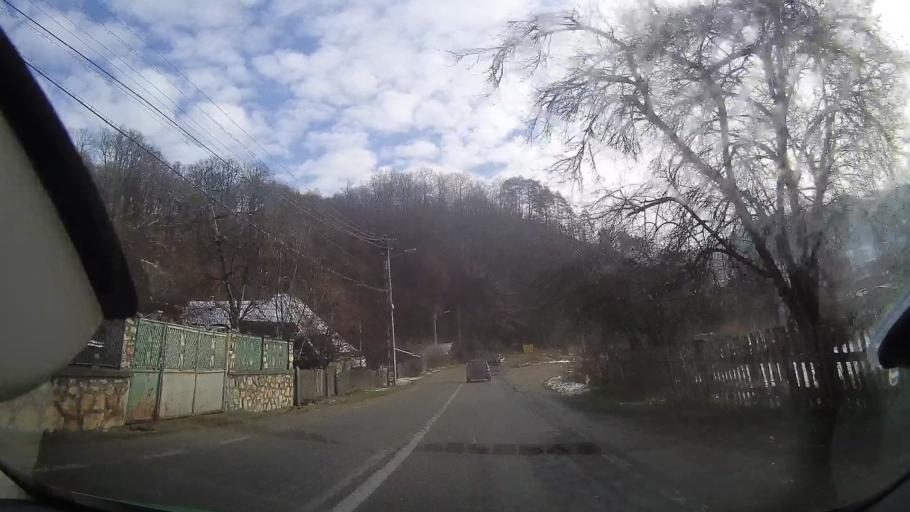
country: RO
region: Alba
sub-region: Oras Baia de Aries
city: Baia de Aries
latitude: 46.3827
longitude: 23.2775
